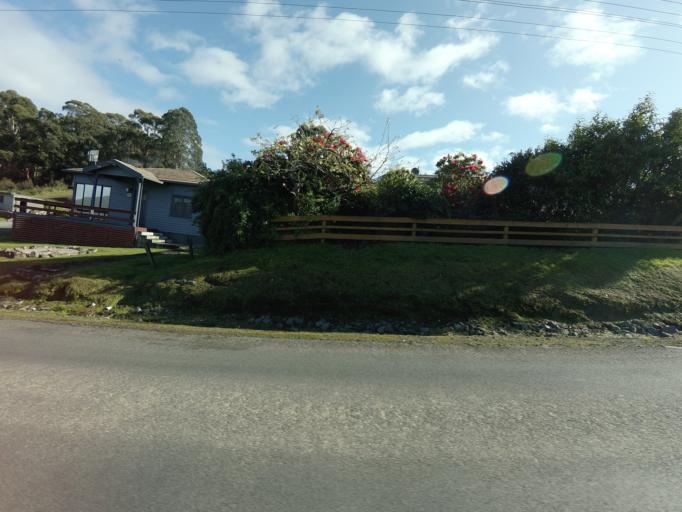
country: AU
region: Tasmania
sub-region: Huon Valley
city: Cygnet
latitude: -43.3148
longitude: 147.0142
